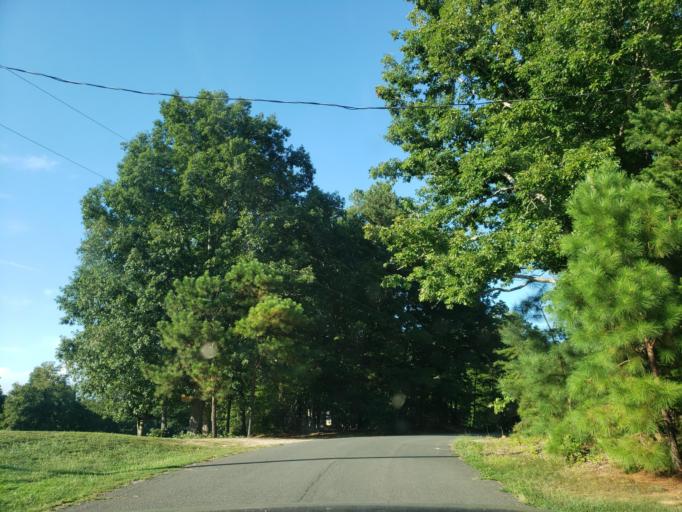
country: US
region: North Carolina
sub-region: Vance County
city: Henderson
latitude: 36.4038
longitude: -78.3817
